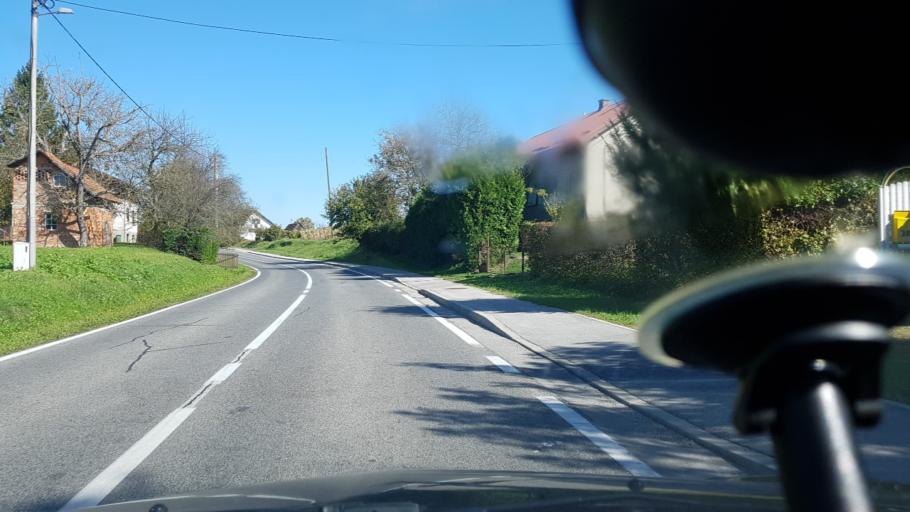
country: HR
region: Zagrebacka
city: Kriz
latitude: 45.7123
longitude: 16.4933
